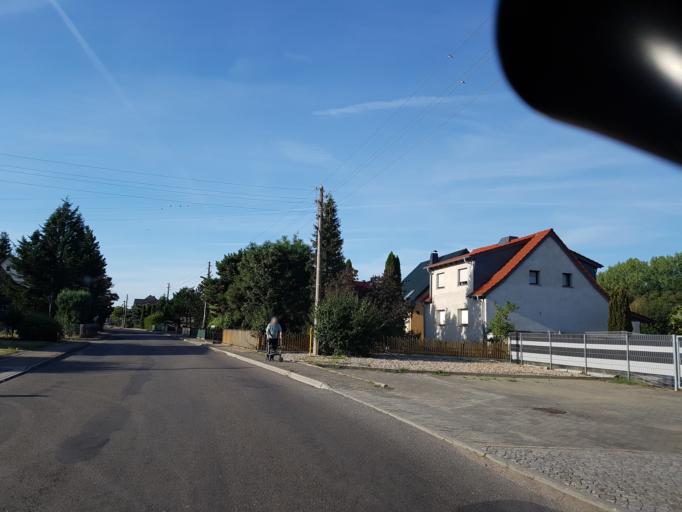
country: DE
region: Saxony
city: Nauwalde
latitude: 51.4432
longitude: 13.4505
